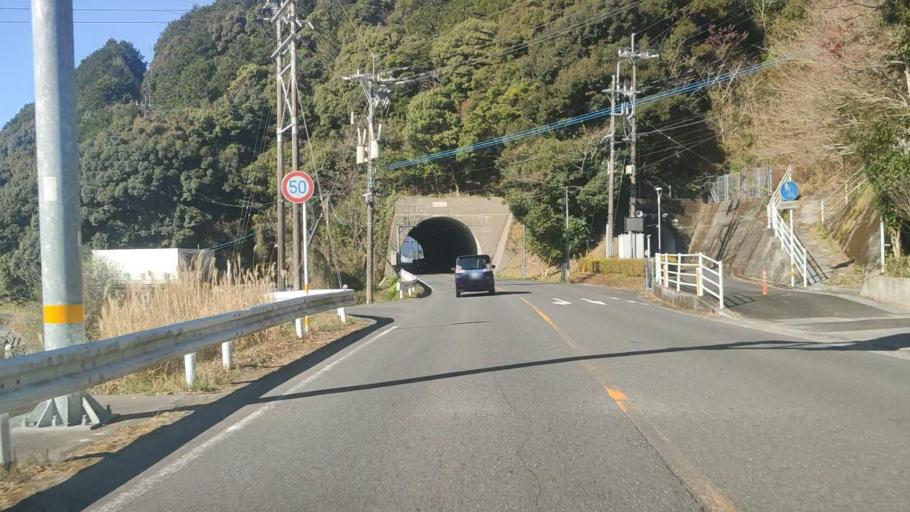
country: JP
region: Oita
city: Saiki
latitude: 32.9420
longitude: 131.9097
